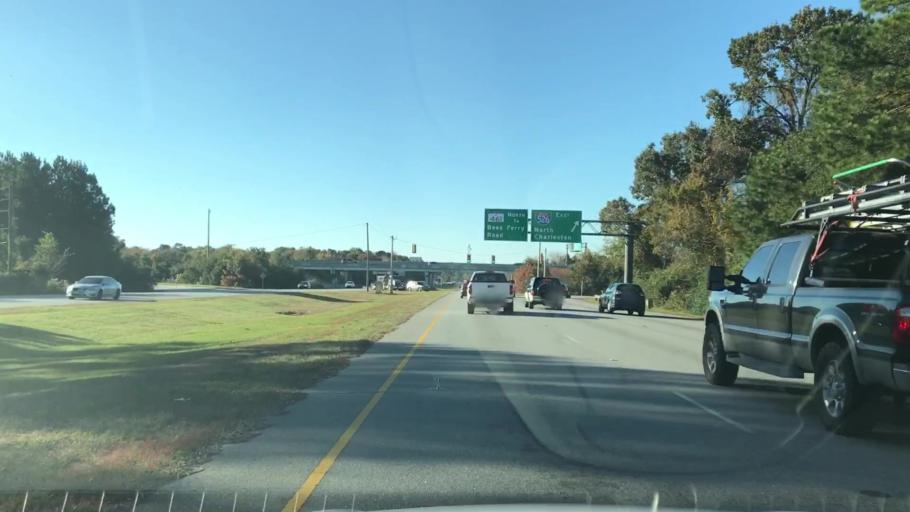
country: US
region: South Carolina
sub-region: Charleston County
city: North Charleston
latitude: 32.8088
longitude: -80.0340
